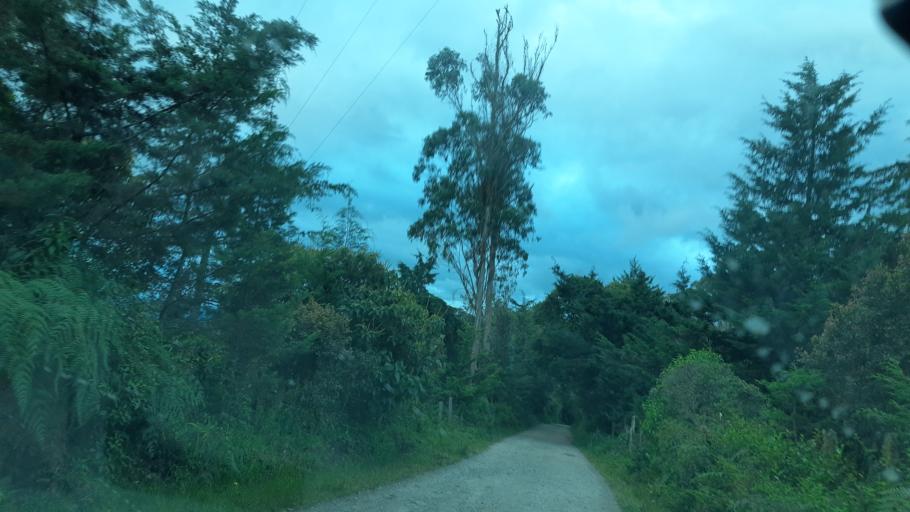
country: CO
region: Boyaca
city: Garagoa
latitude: 5.0908
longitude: -73.3309
